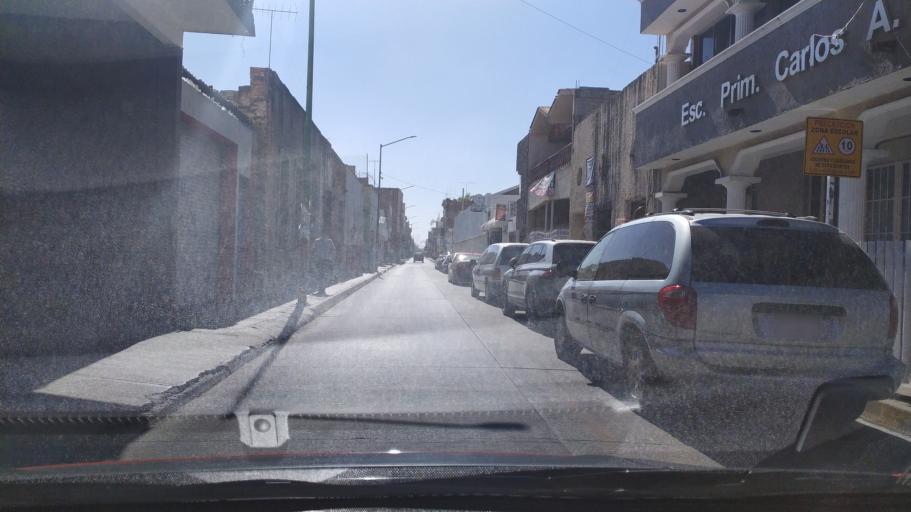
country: MX
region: Guanajuato
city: San Francisco del Rincon
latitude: 21.0212
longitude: -101.8578
